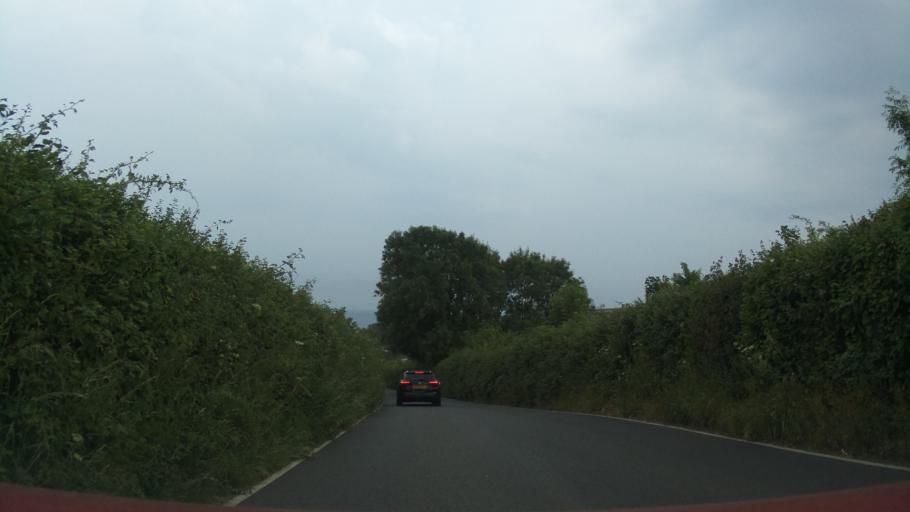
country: GB
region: England
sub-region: Devon
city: Colyton
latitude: 50.7062
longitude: -3.1011
